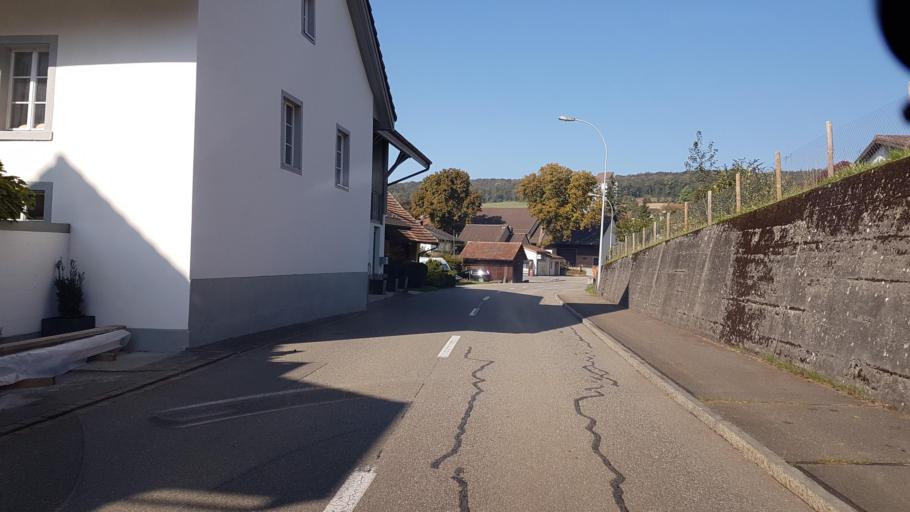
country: CH
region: Aargau
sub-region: Bezirk Brugg
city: Villnachern
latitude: 47.5165
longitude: 8.1454
